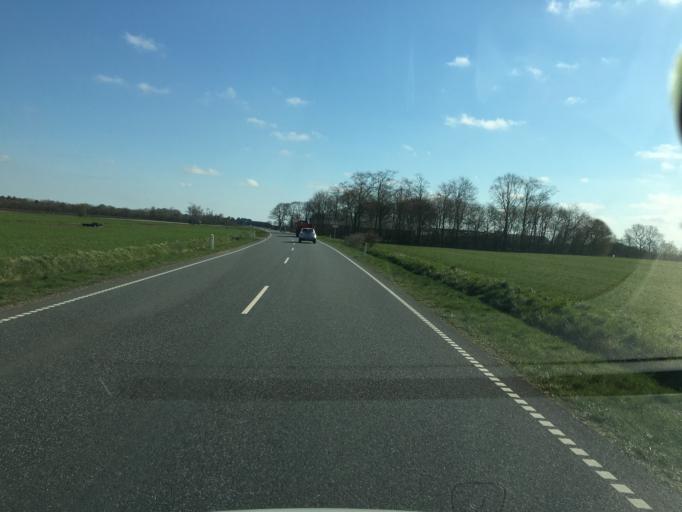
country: DK
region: South Denmark
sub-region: Tonder Kommune
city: Toftlund
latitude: 55.0594
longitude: 9.1346
